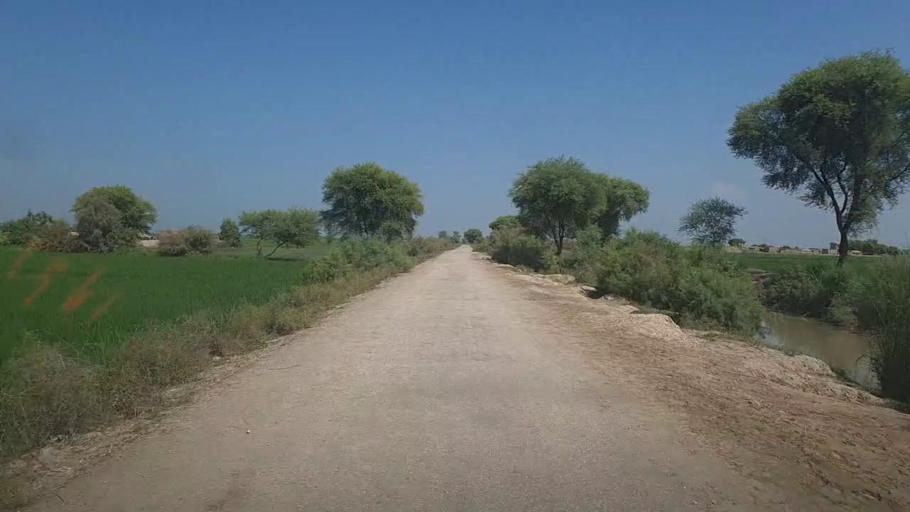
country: PK
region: Sindh
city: Kandhkot
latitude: 28.2974
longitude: 69.1984
